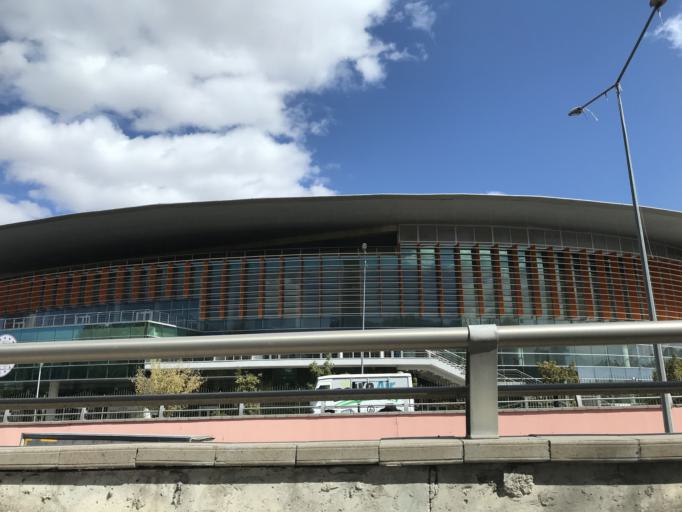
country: TR
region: Ankara
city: Ankara
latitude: 39.9371
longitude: 32.8435
